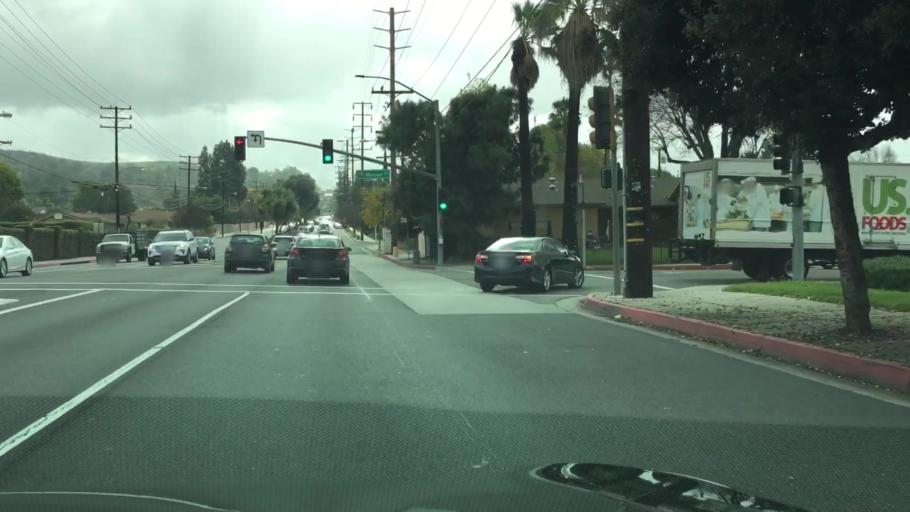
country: US
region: California
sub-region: Los Angeles County
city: West Covina
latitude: 34.0541
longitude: -117.9081
